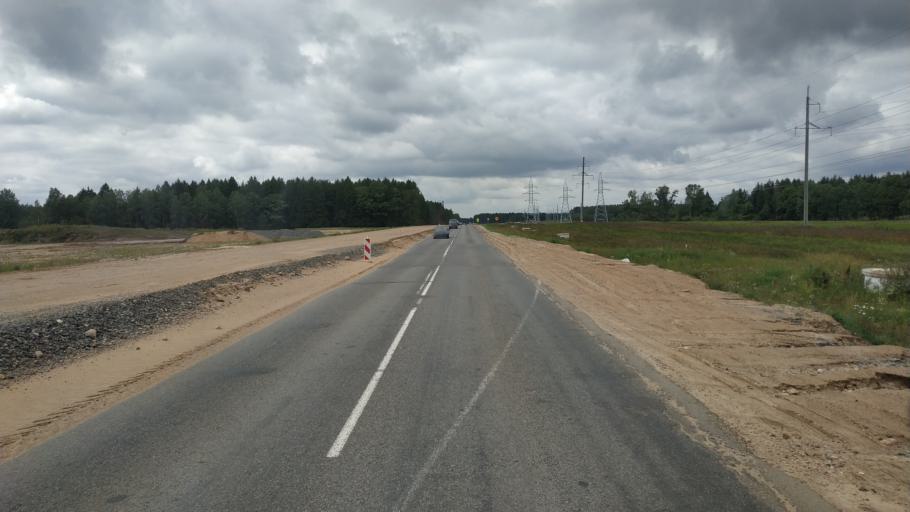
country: BY
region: Mogilev
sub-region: Mahilyowski Rayon
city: Kadino
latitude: 53.8725
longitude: 30.4489
